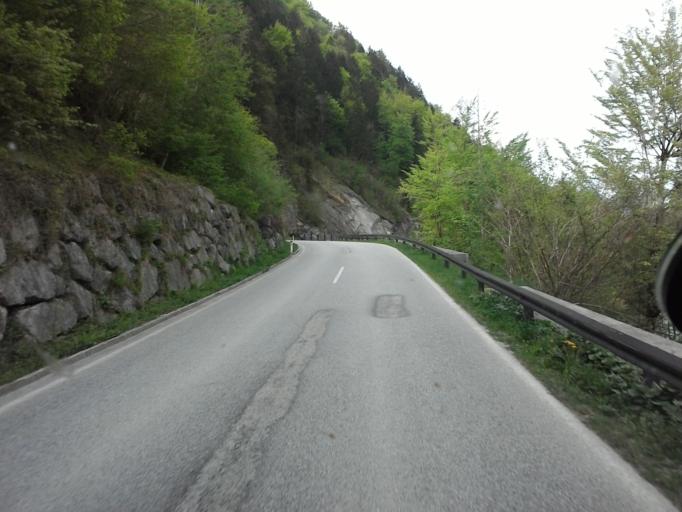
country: AT
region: Styria
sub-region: Politischer Bezirk Liezen
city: Gams bei Hieflau
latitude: 47.6834
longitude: 14.7686
